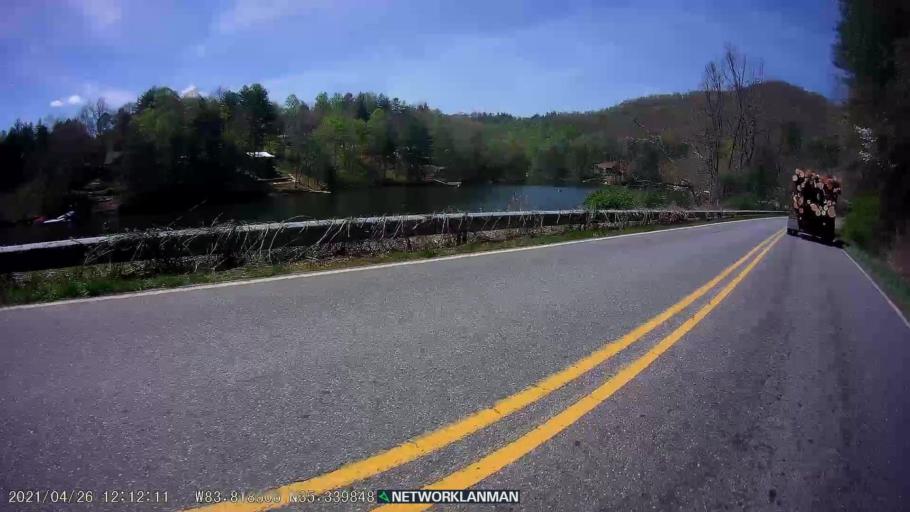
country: US
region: North Carolina
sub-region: Graham County
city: Robbinsville
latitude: 35.3402
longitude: -83.8185
